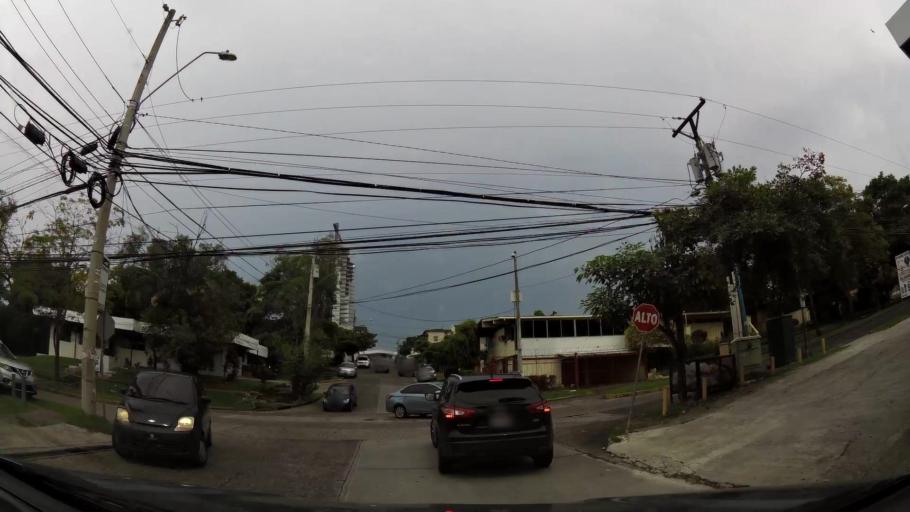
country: PA
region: Panama
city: Panama
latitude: 8.9978
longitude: -79.5325
